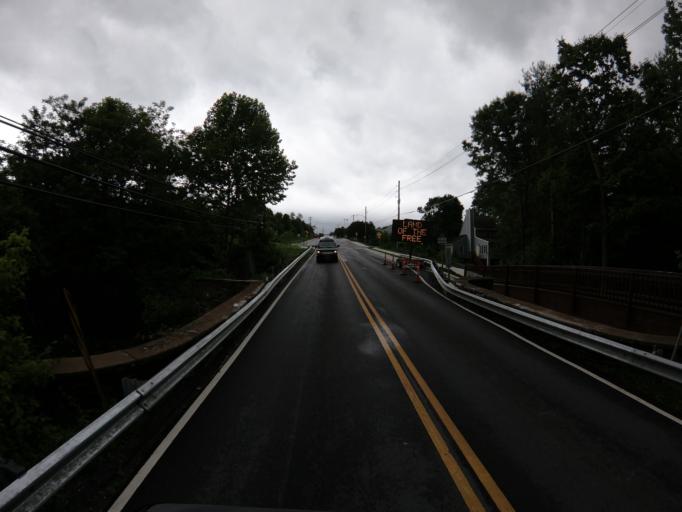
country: US
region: Maryland
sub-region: Frederick County
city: Middletown
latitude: 39.4460
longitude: -77.5553
